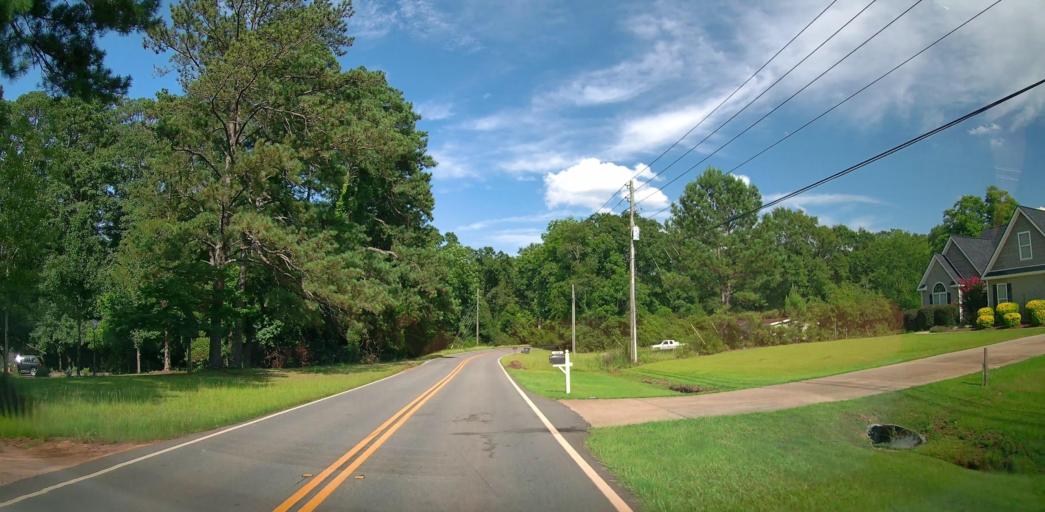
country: US
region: Georgia
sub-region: Houston County
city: Centerville
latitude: 32.5381
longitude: -83.6773
